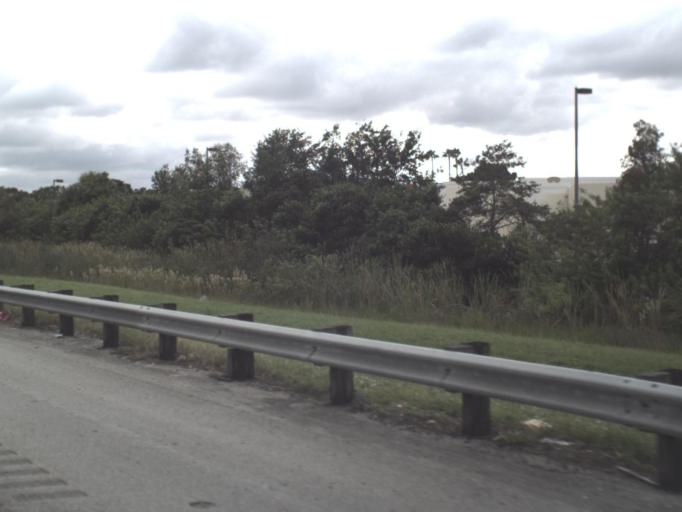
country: US
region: Florida
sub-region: Palm Beach County
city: Palm Beach Gardens
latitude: 26.8369
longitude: -80.1302
